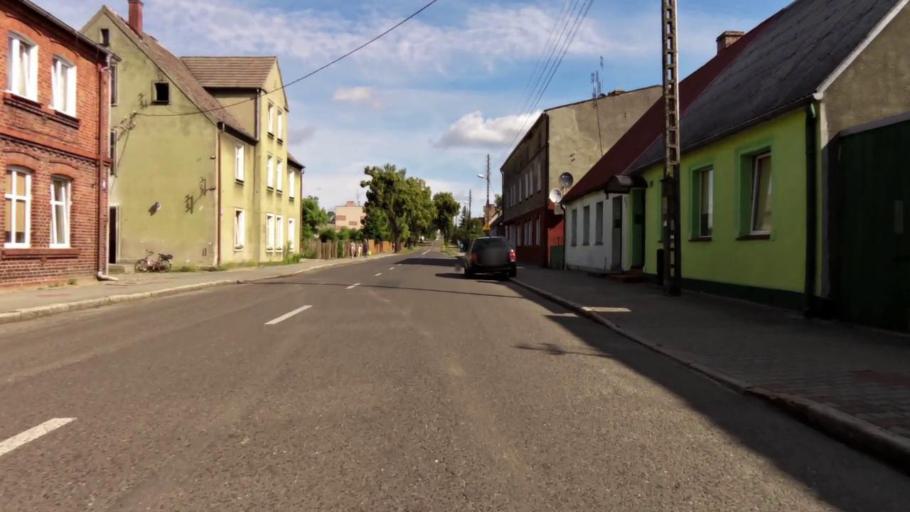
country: PL
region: West Pomeranian Voivodeship
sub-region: Powiat stargardzki
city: Dobrzany
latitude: 53.3607
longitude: 15.4286
